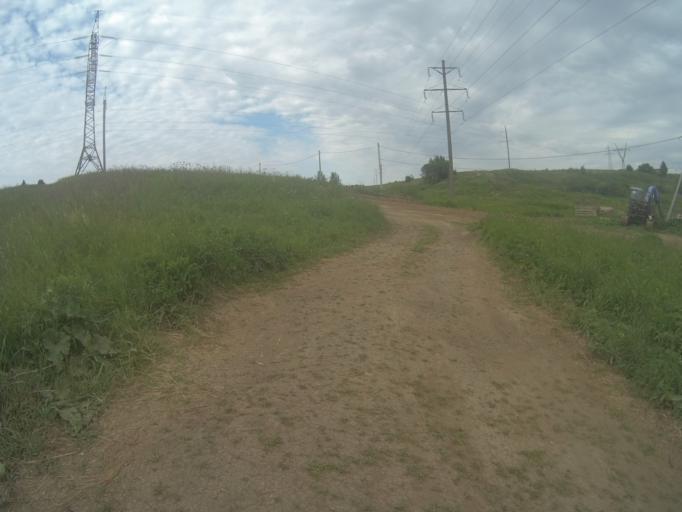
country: RU
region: Vladimir
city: Bogolyubovo
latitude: 56.1852
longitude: 40.5035
